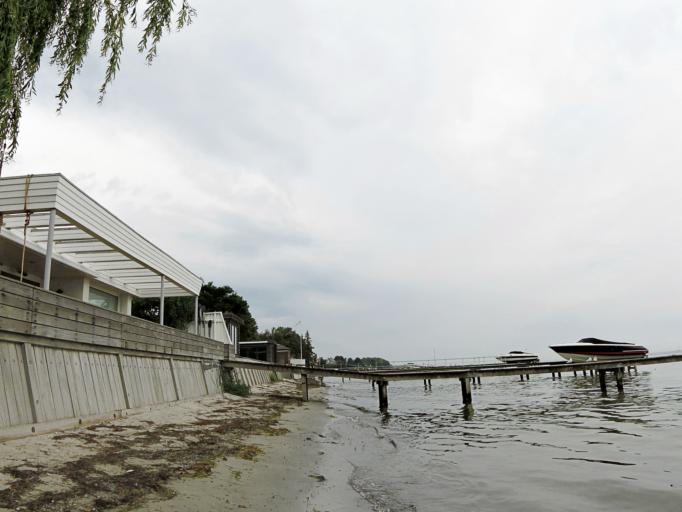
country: DK
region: Capital Region
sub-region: Gentofte Kommune
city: Charlottenlund
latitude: 55.7361
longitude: 12.5828
